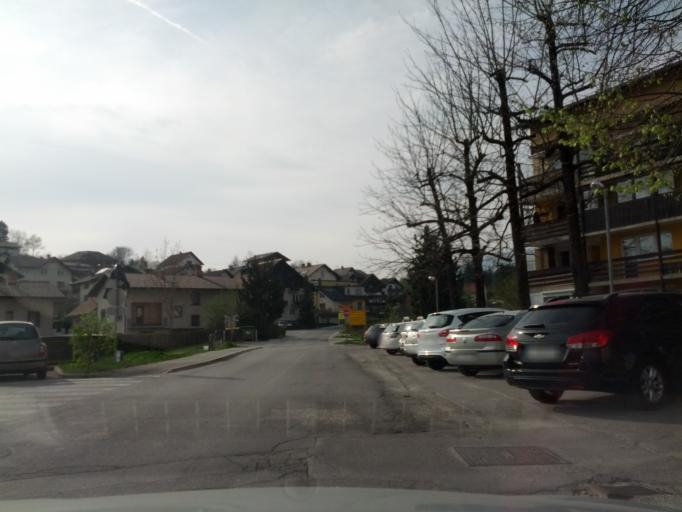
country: SI
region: Kamnik
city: Kamnik
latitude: 46.2295
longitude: 14.6100
